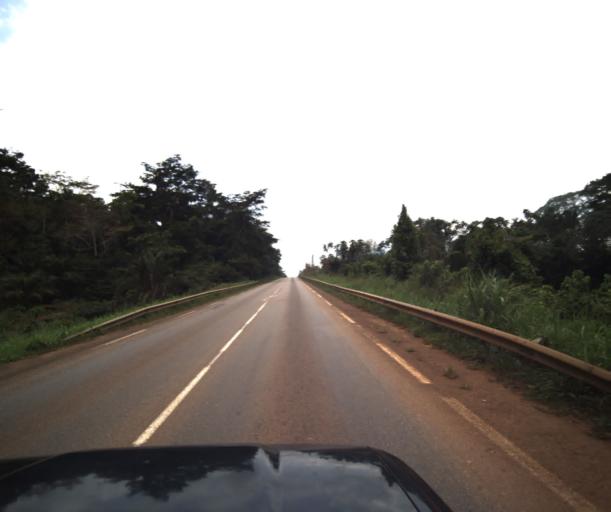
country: CM
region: Centre
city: Eseka
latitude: 3.8639
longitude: 10.9228
